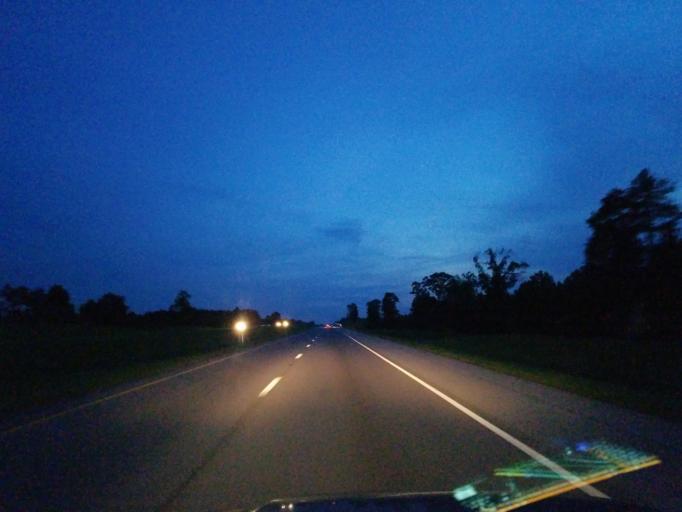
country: US
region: Mississippi
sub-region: Jones County
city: Ellisville
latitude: 31.5568
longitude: -89.2601
